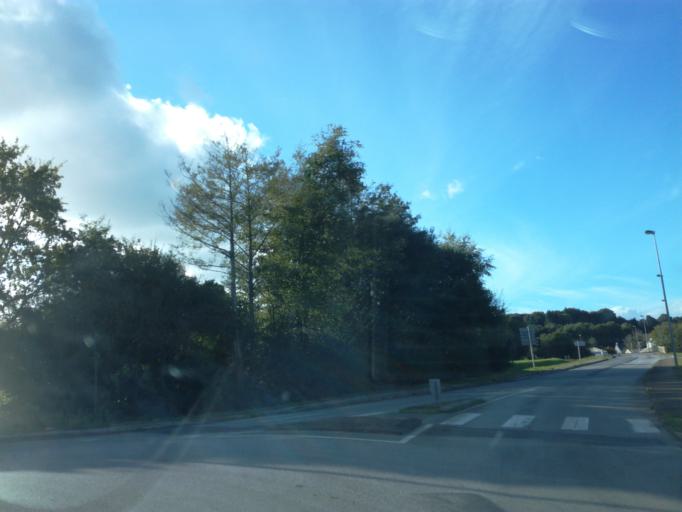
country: FR
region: Brittany
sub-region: Departement du Morbihan
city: Le Sourn
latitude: 48.0411
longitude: -2.9640
